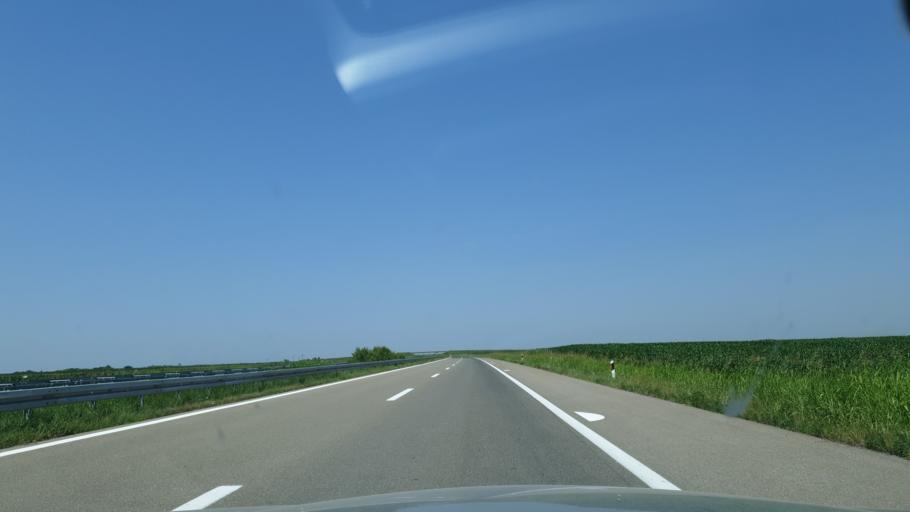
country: RS
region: Autonomna Pokrajina Vojvodina
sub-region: Severnobacki Okrug
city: Backa Topola
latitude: 45.8632
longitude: 19.6994
